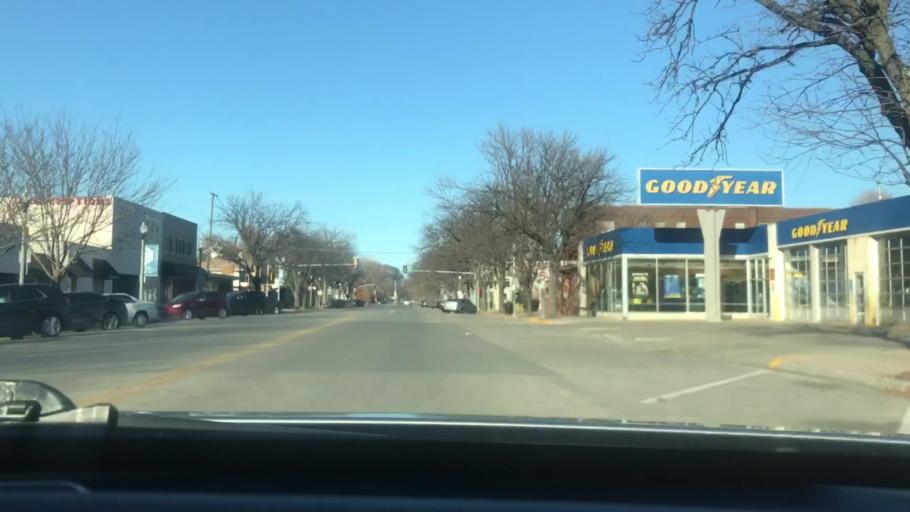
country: US
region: Missouri
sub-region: Clay County
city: North Kansas City
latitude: 39.1429
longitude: -94.5771
